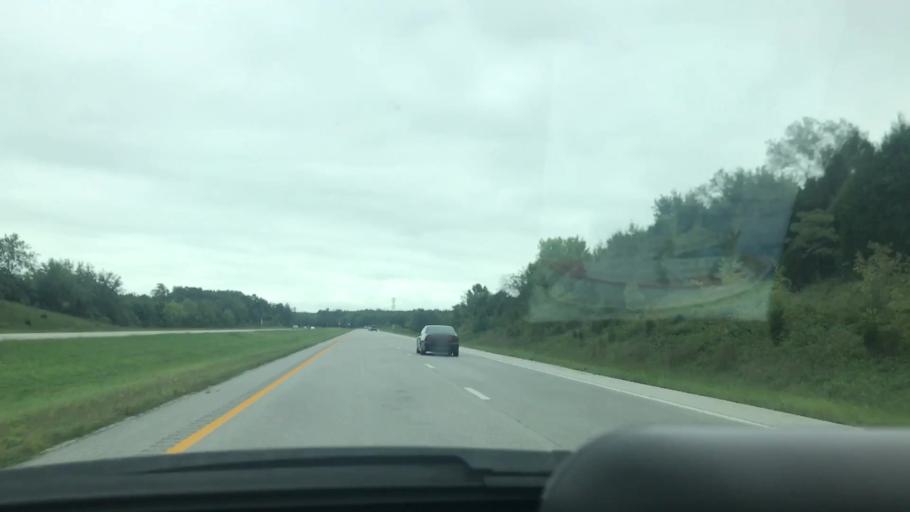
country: US
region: Missouri
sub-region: Greene County
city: Strafford
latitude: 37.3148
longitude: -93.1706
